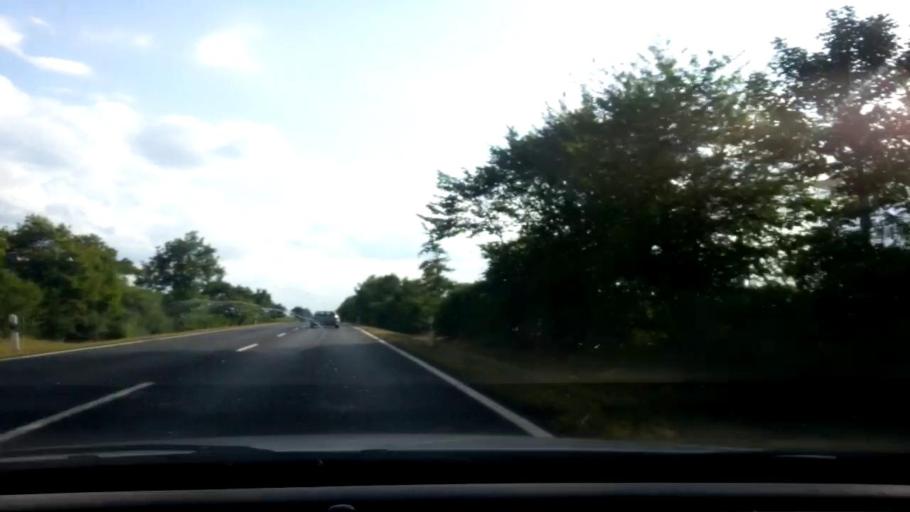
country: DE
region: Bavaria
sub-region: Upper Palatinate
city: Waldsassen
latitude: 49.9873
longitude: 12.2815
